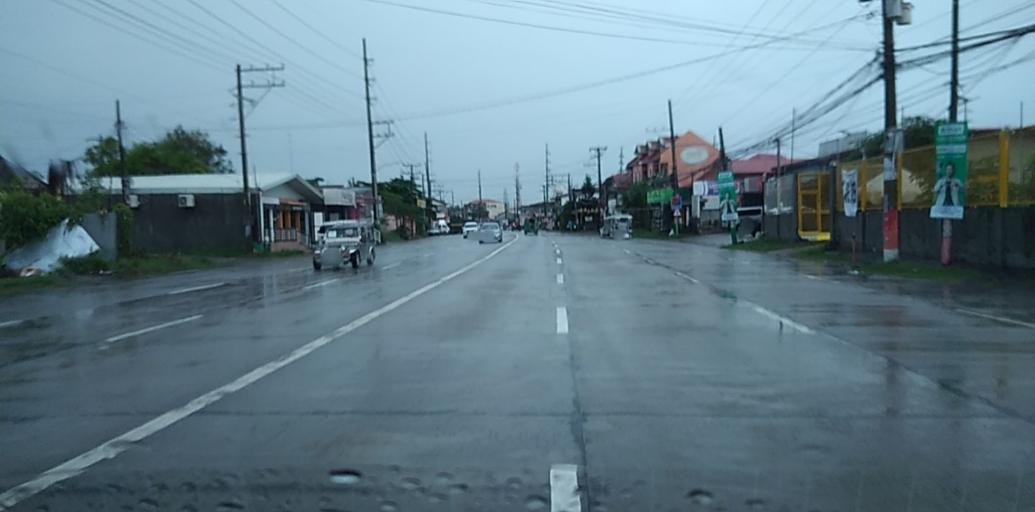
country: PH
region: Central Luzon
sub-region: Province of Pampanga
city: Mexico
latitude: 15.0525
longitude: 120.7081
